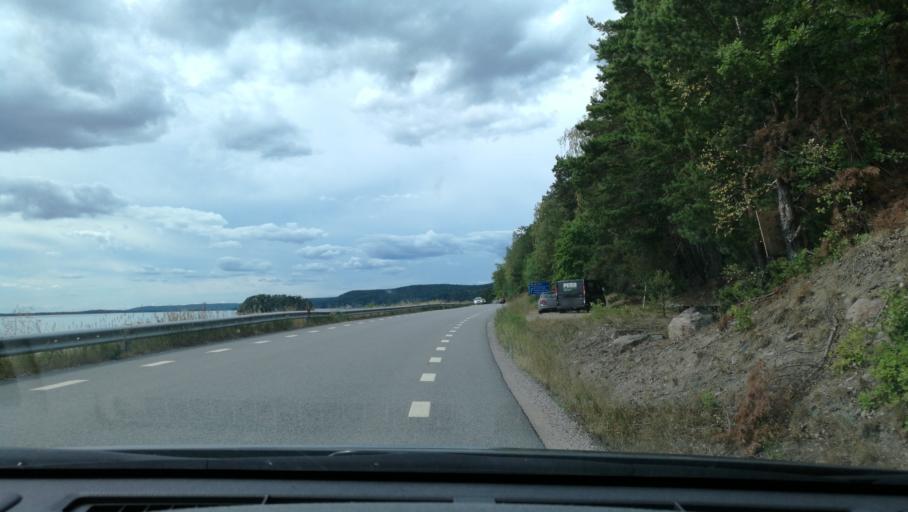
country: SE
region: OEstergoetland
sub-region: Norrkopings Kommun
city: Krokek
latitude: 58.6596
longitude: 16.3790
